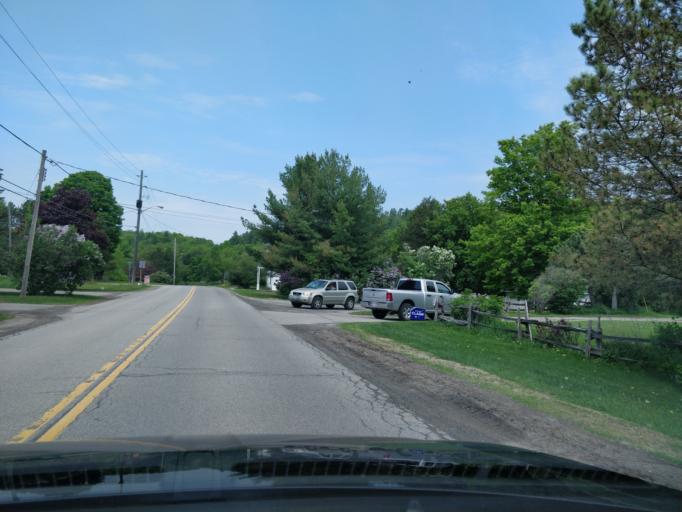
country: CA
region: Ontario
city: Perth
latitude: 44.6824
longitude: -76.4076
